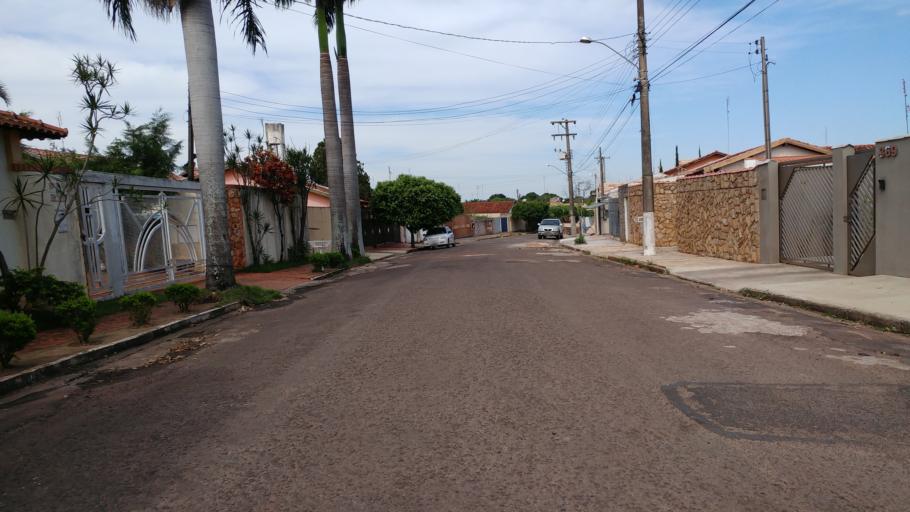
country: BR
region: Sao Paulo
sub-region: Paraguacu Paulista
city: Paraguacu Paulista
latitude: -22.4052
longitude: -50.5786
